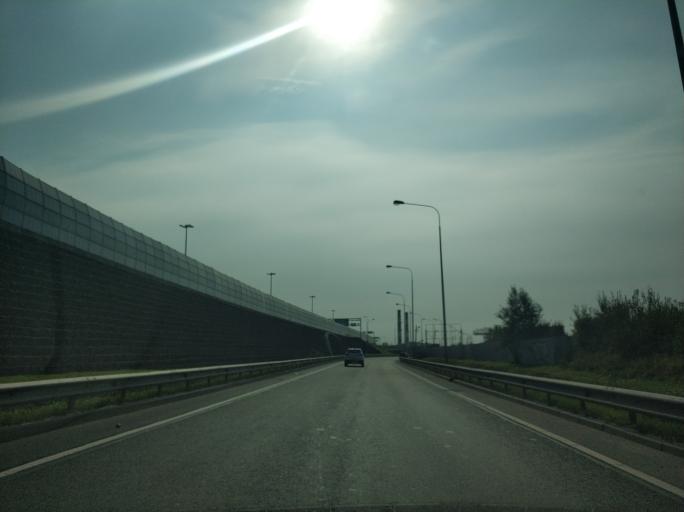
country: RU
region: Leningrad
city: Murino
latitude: 60.0389
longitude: 30.4386
